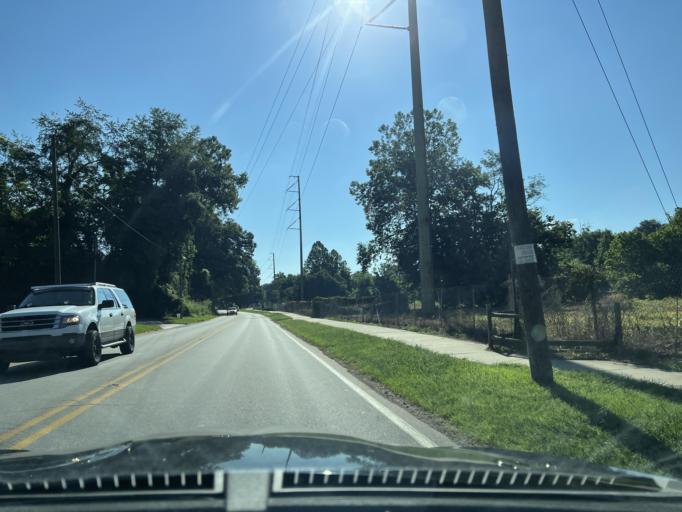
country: US
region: North Carolina
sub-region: Buncombe County
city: Asheville
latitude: 35.5667
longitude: -82.5734
